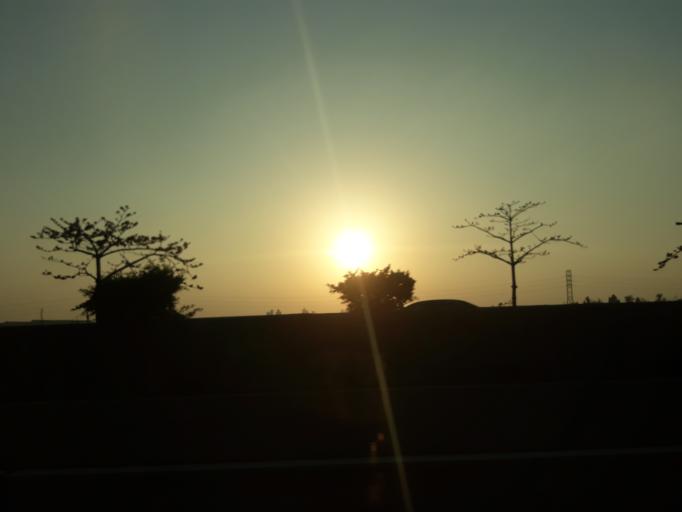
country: TW
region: Taiwan
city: Fengshan
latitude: 22.7685
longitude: 120.3278
